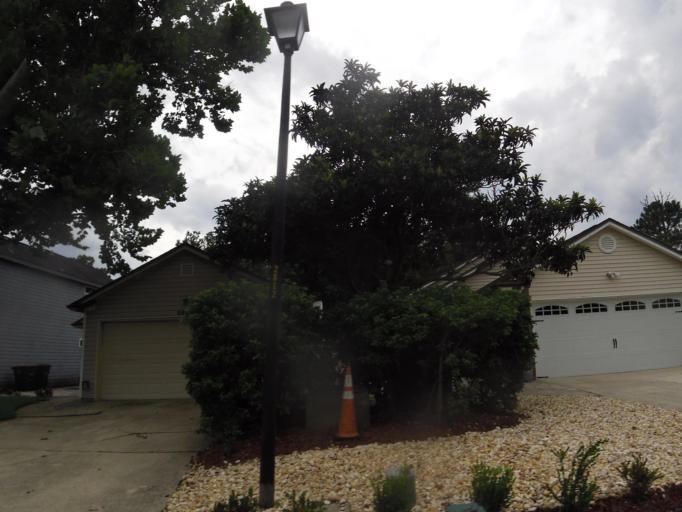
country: US
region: Florida
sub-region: Duval County
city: Jacksonville
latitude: 30.2954
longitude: -81.5438
